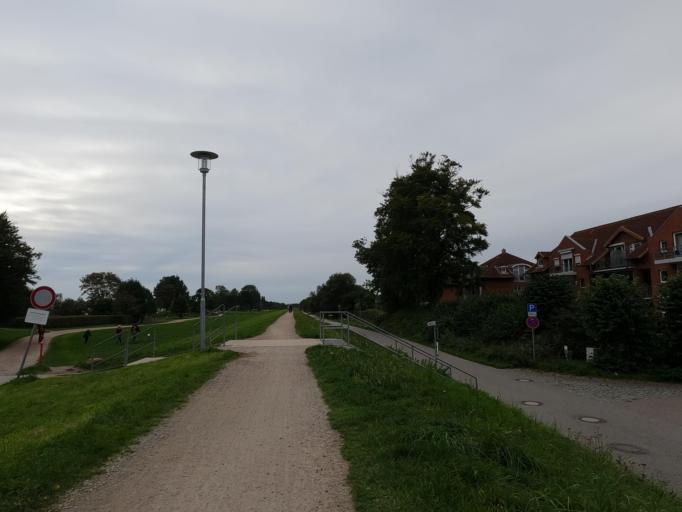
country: DE
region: Schleswig-Holstein
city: Kellenhusen
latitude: 54.1870
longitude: 11.0590
